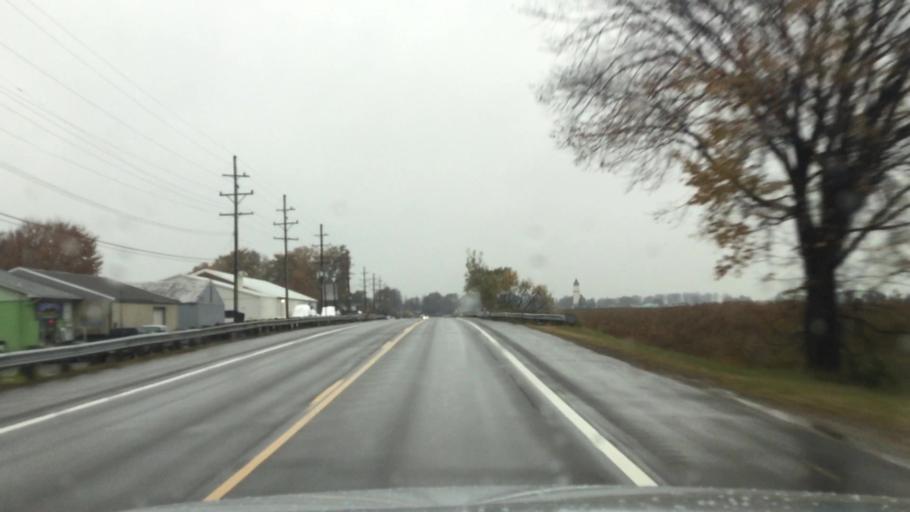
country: US
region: Michigan
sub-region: Saint Clair County
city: Pearl Beach
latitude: 42.6281
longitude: -82.6045
